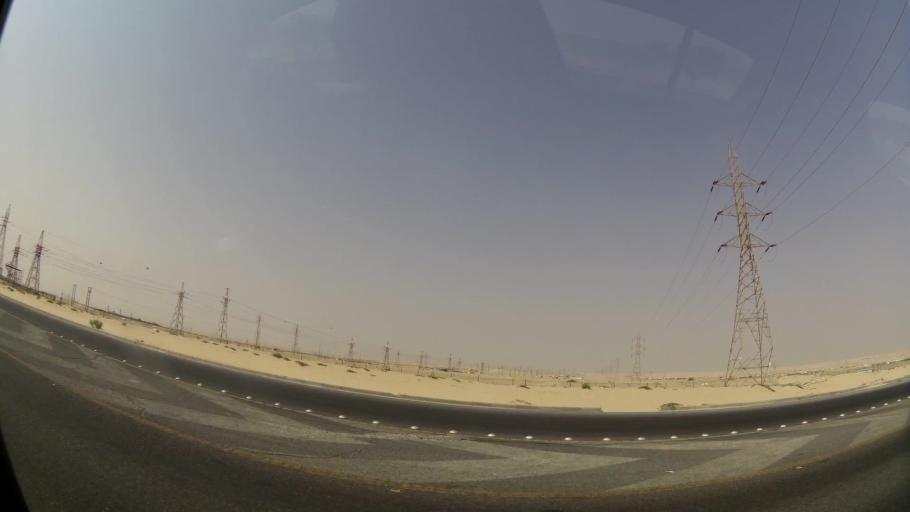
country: KW
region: Muhafazat al Jahra'
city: Al Jahra'
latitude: 29.3476
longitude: 47.6305
